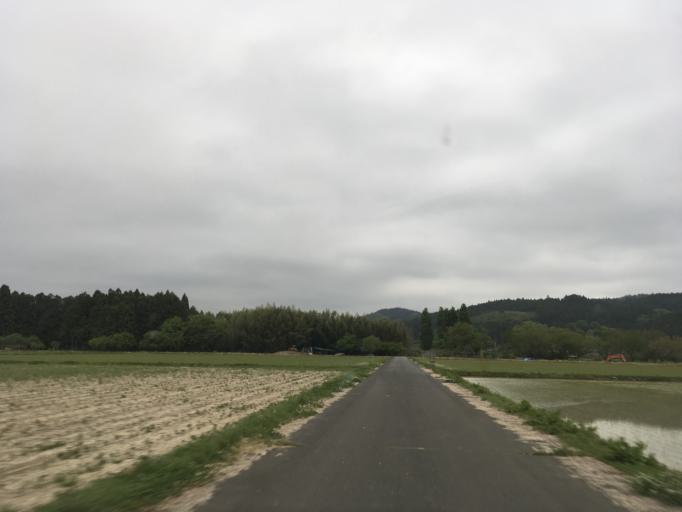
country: JP
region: Miyagi
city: Wakuya
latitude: 38.7165
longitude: 141.2902
